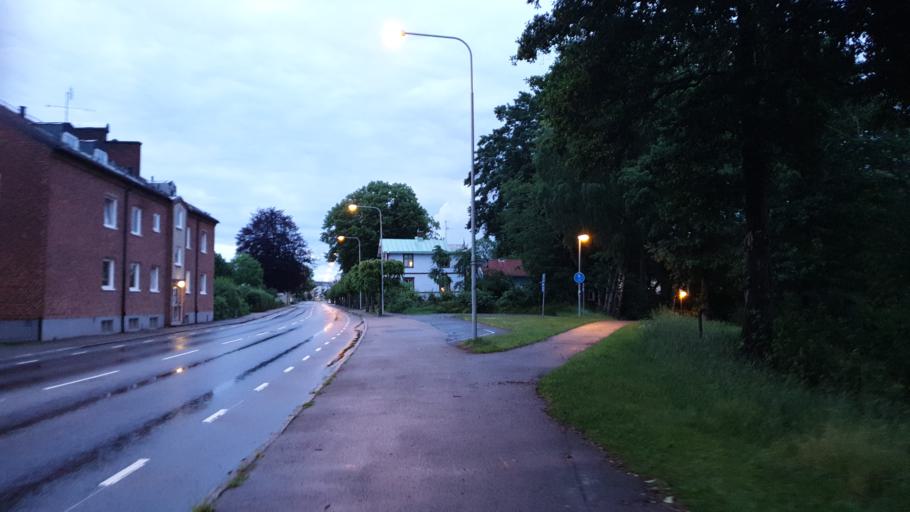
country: SE
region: Kronoberg
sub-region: Ljungby Kommun
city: Ljungby
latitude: 56.8293
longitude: 13.9385
